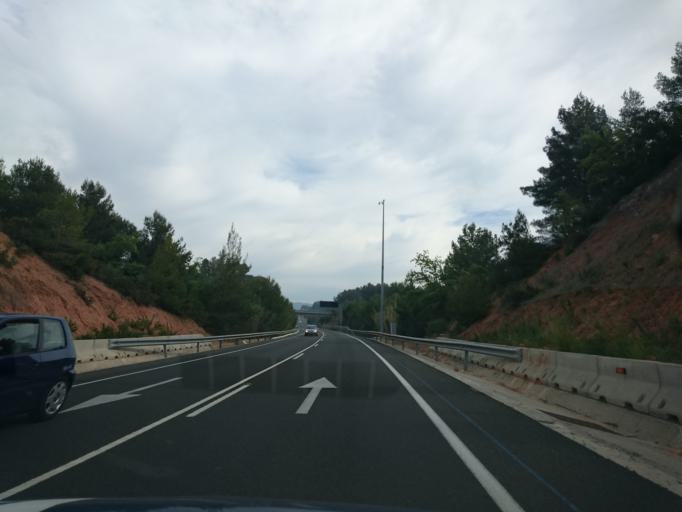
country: ES
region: Catalonia
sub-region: Provincia de Barcelona
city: Sant Pere de Riudebitlles
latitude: 41.4850
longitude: 1.7022
